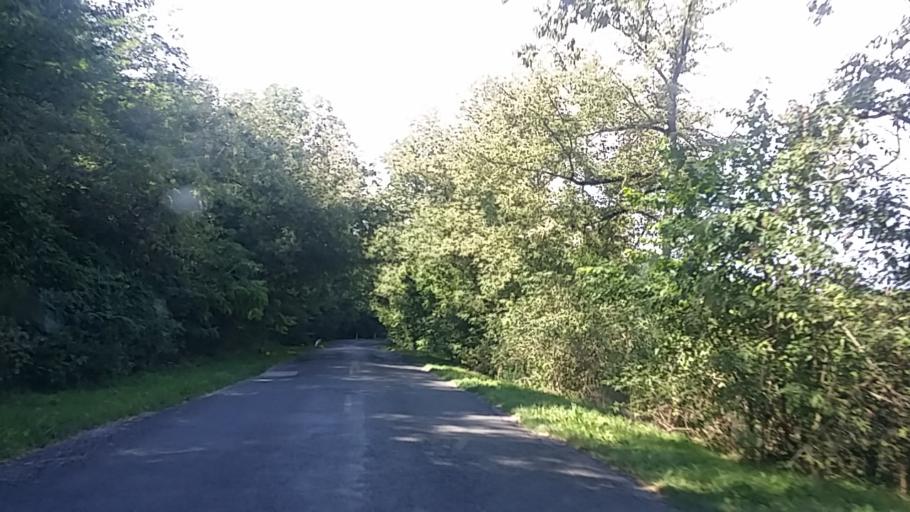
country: HU
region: Tolna
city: Hogyesz
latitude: 46.5223
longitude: 18.4250
